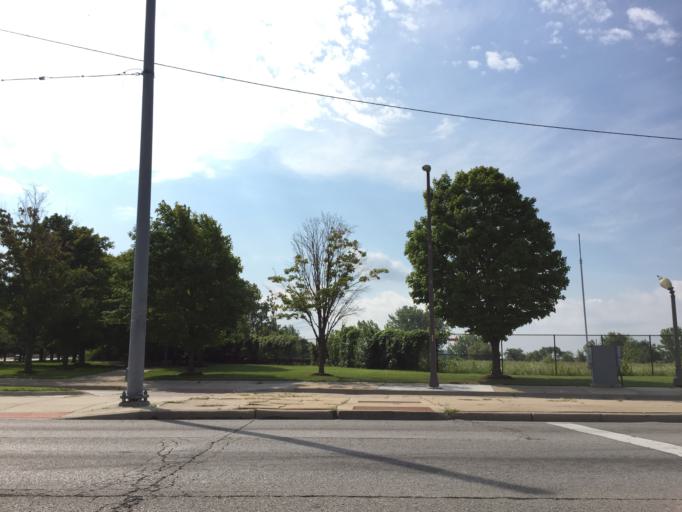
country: US
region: Michigan
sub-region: Wayne County
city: Detroit
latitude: 42.3465
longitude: -83.0030
